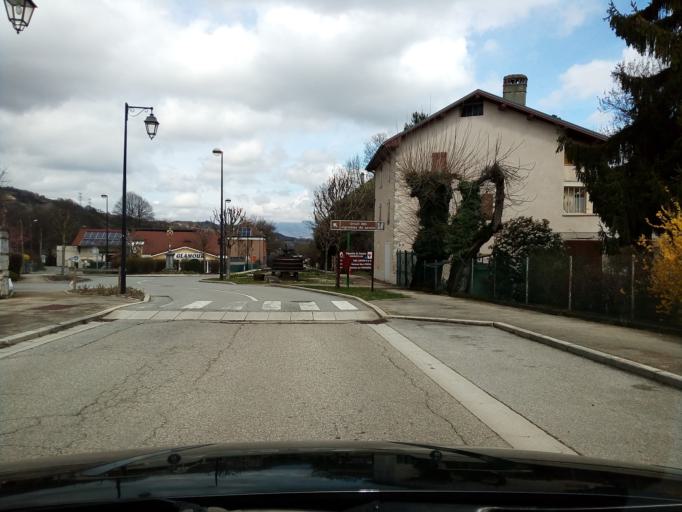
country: FR
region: Rhone-Alpes
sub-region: Departement de l'Isere
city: Chapareillan
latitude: 45.4679
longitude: 5.9897
